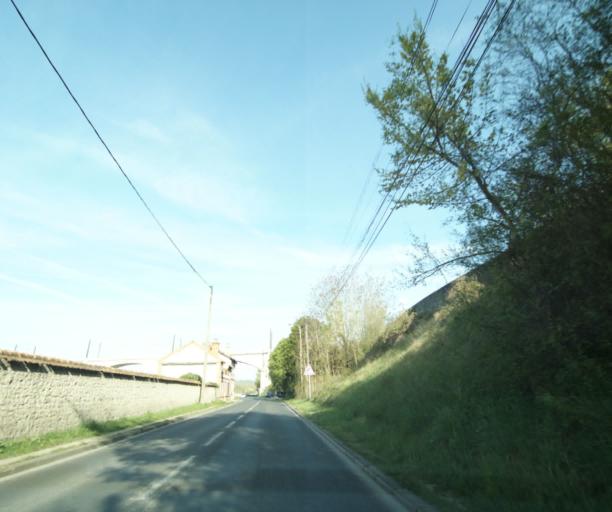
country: FR
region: Ile-de-France
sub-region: Departement de Seine-et-Marne
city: Saint-Mammes
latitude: 48.3801
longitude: 2.8149
